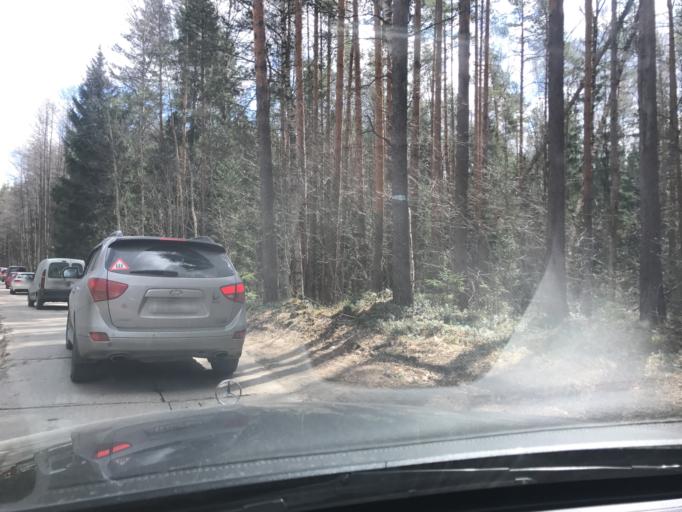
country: RU
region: Moskovskaya
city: Vereya
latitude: 55.8391
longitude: 39.1130
